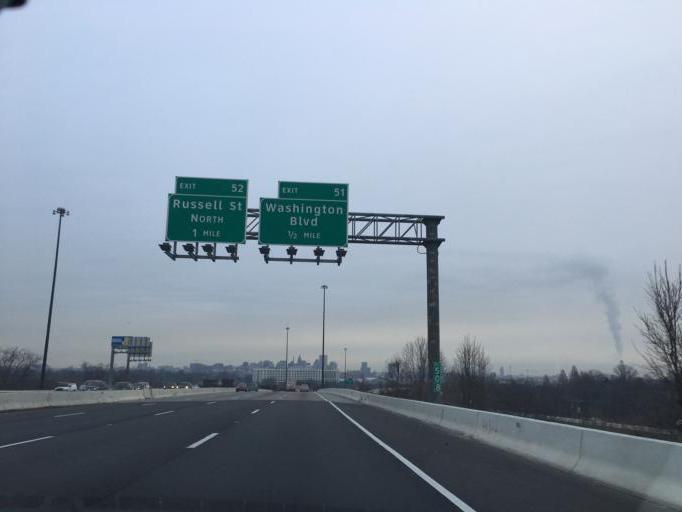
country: US
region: Maryland
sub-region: Baltimore County
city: Lansdowne
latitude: 39.2697
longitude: -76.6579
